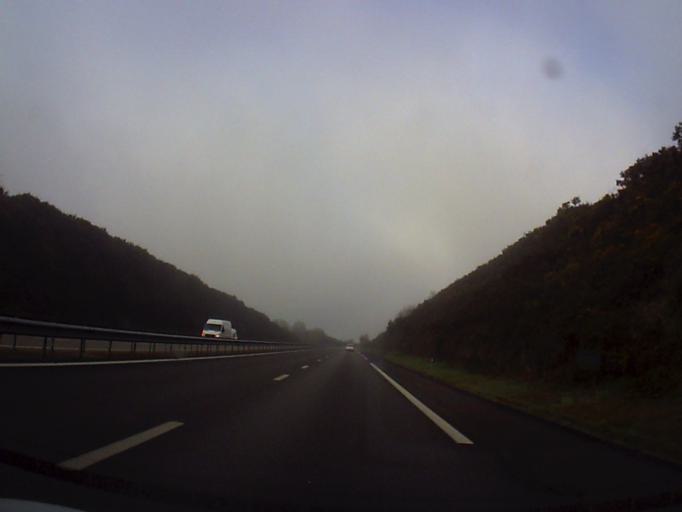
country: FR
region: Brittany
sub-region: Departement du Morbihan
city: Guer
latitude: 47.9246
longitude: -2.1625
